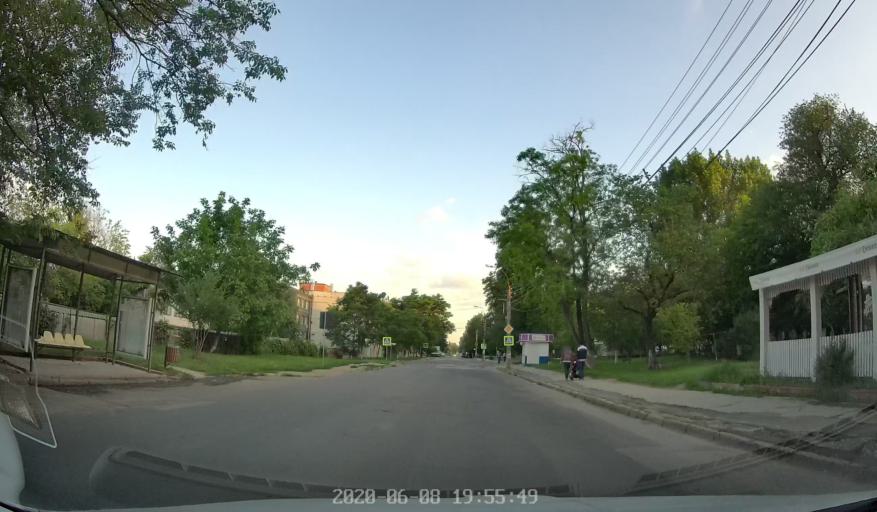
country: MD
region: Chisinau
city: Chisinau
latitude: 47.0262
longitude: 28.8836
